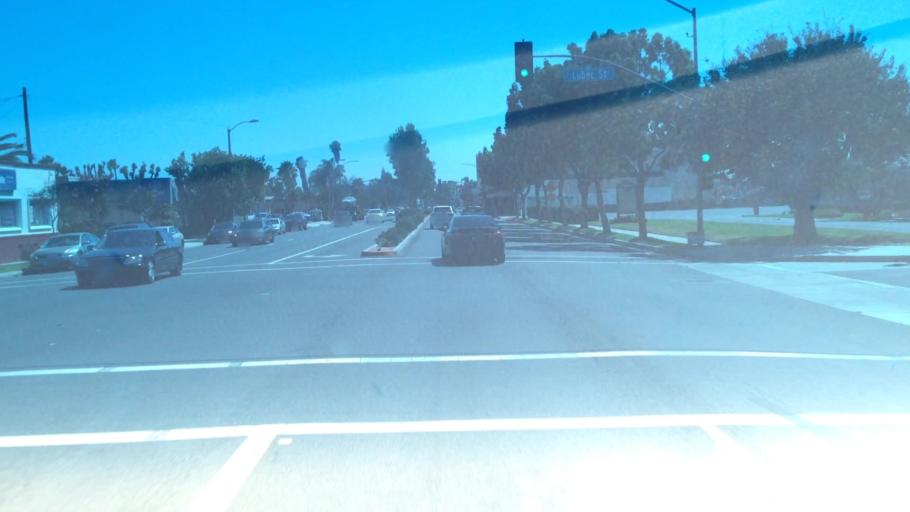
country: US
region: California
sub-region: Los Angeles County
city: Downey
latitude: 33.9569
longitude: -118.1275
